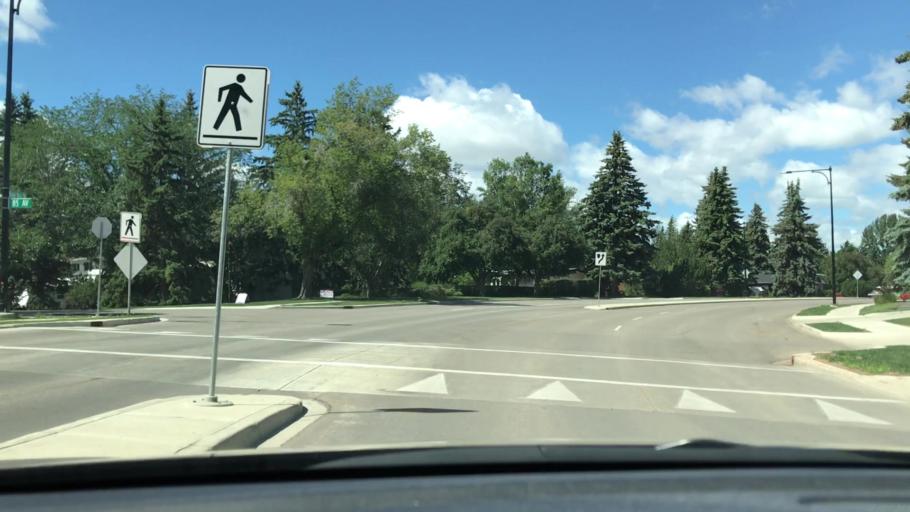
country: CA
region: Alberta
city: Edmonton
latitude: 53.5172
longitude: -113.5589
